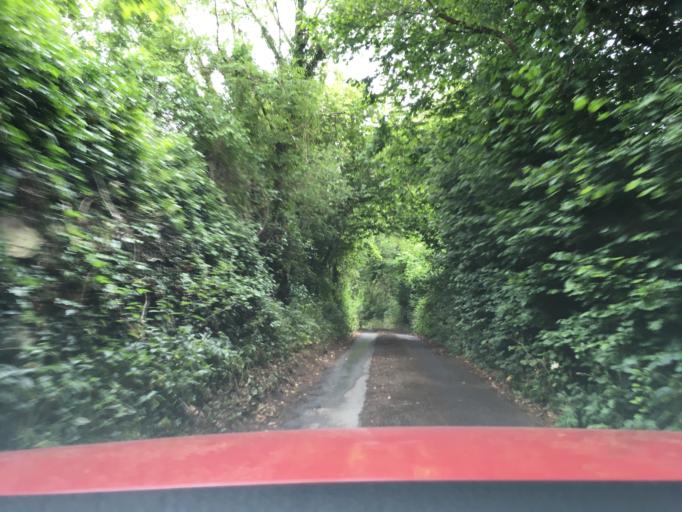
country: GB
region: England
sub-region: Gloucestershire
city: Shurdington
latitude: 51.7976
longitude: -2.0818
